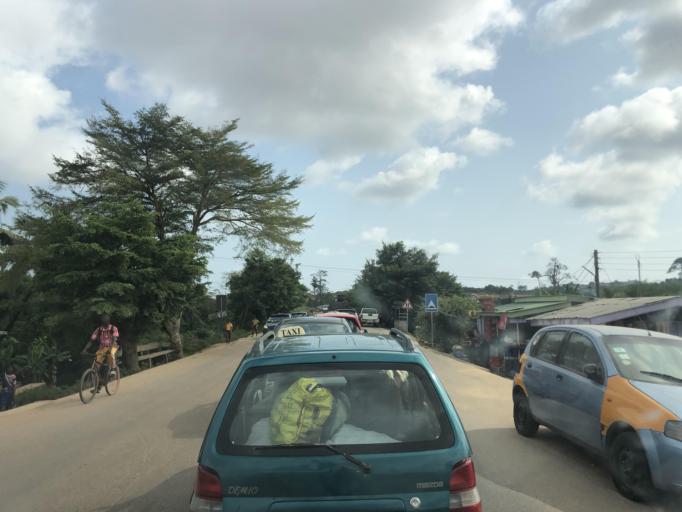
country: GH
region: Central
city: Cape Coast
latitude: 5.1487
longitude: -1.2880
